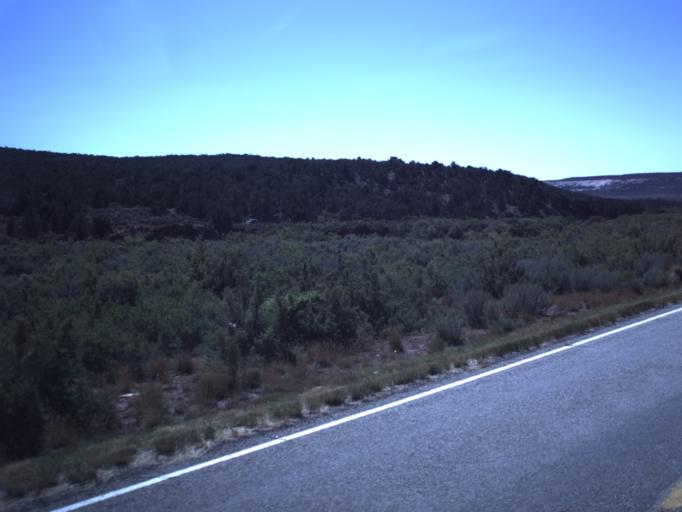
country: US
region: Utah
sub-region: Grand County
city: Moab
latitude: 38.3164
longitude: -109.3497
